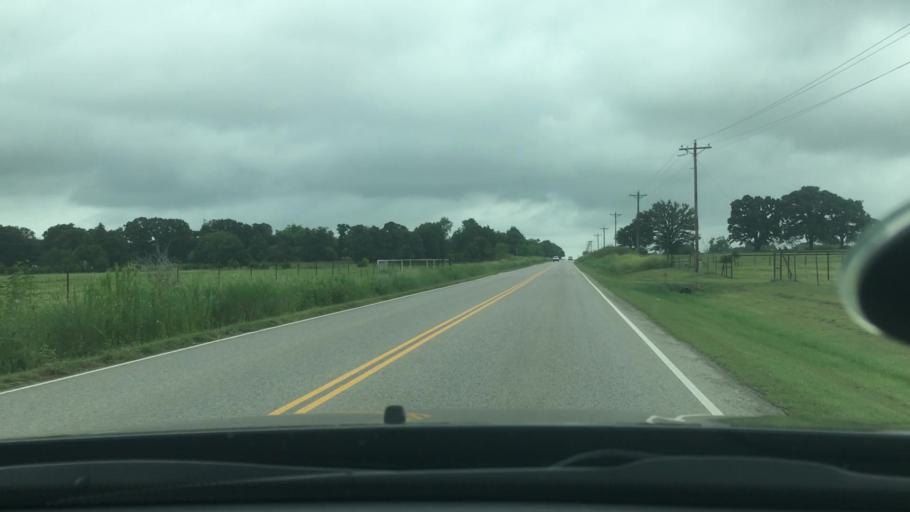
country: US
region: Oklahoma
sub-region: Bryan County
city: Calera
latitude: 33.9447
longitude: -96.5005
